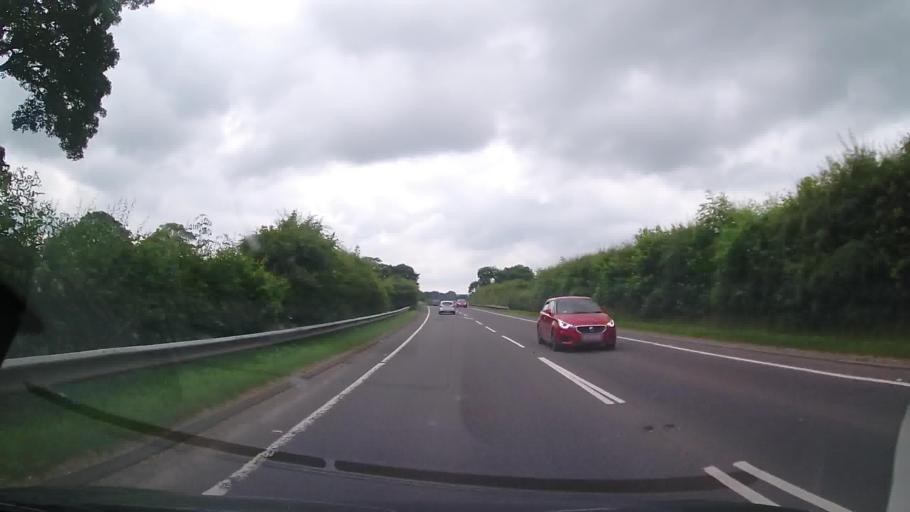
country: GB
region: Wales
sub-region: Denbighshire
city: Corwen
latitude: 52.9819
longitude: -3.4144
